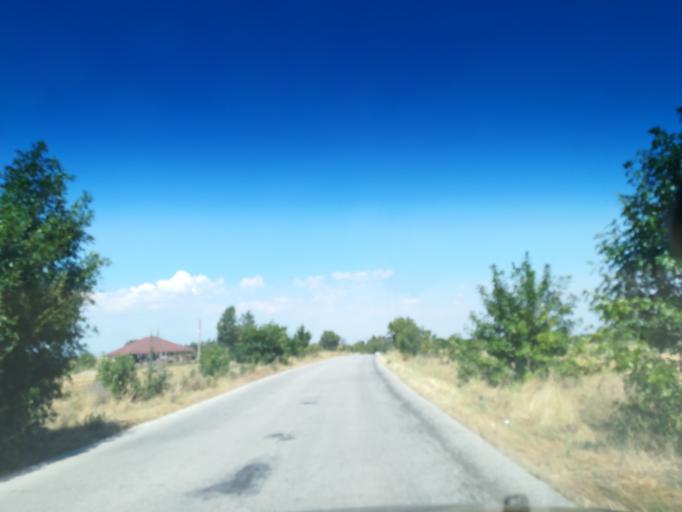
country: BG
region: Stara Zagora
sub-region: Obshtina Chirpan
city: Chirpan
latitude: 42.0589
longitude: 25.1579
